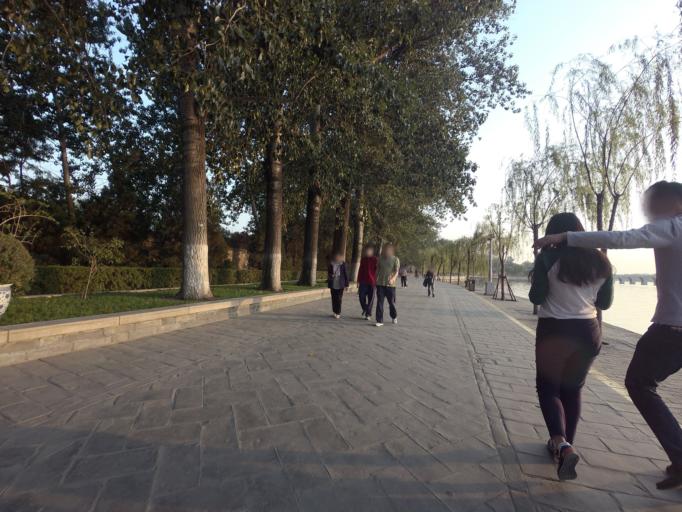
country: CN
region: Beijing
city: Haidian
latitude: 39.9918
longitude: 116.2743
